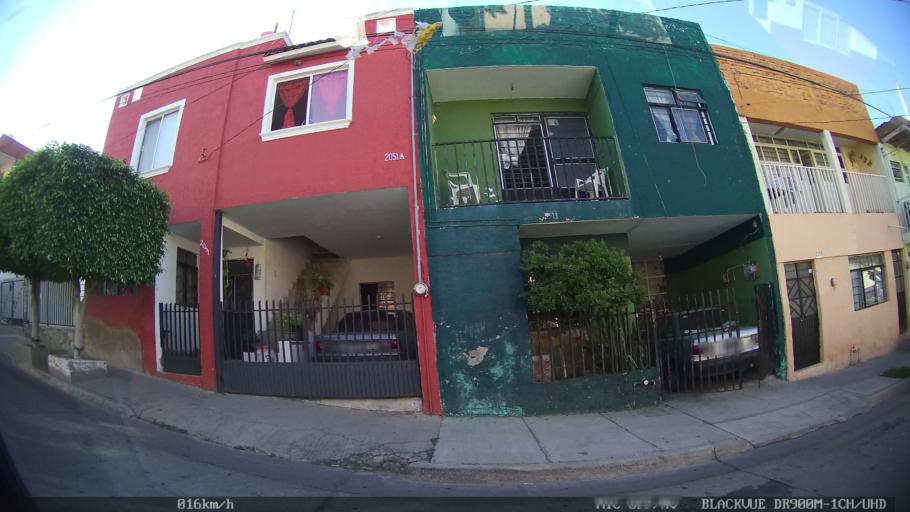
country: MX
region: Jalisco
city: Tlaquepaque
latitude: 20.7024
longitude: -103.2904
